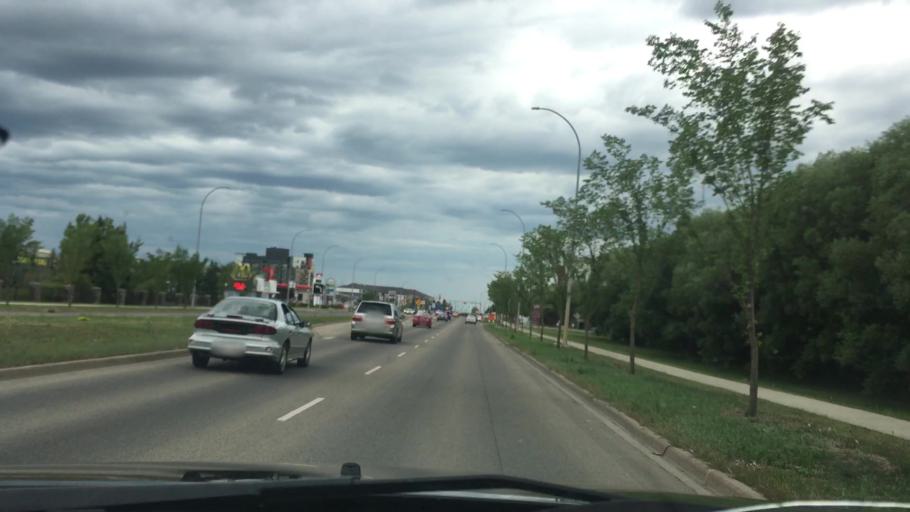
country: CA
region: Alberta
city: Beaumont
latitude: 53.4249
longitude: -113.5113
